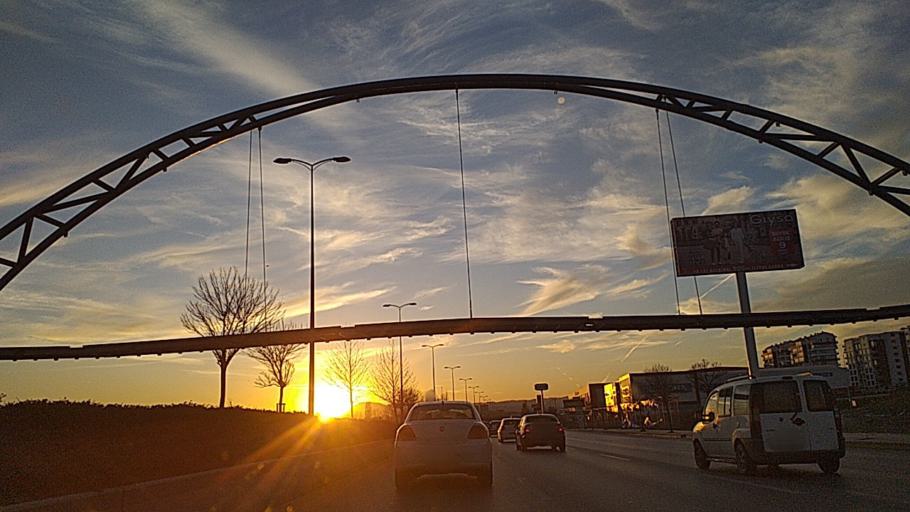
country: TR
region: Ankara
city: Etimesgut
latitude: 39.9628
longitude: 32.6579
